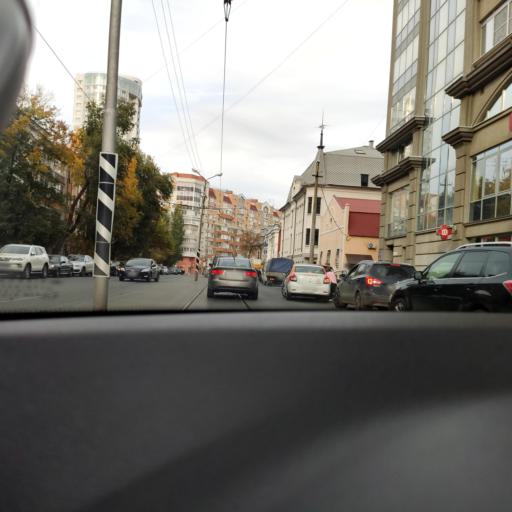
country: RU
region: Samara
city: Samara
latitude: 53.1981
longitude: 50.1065
